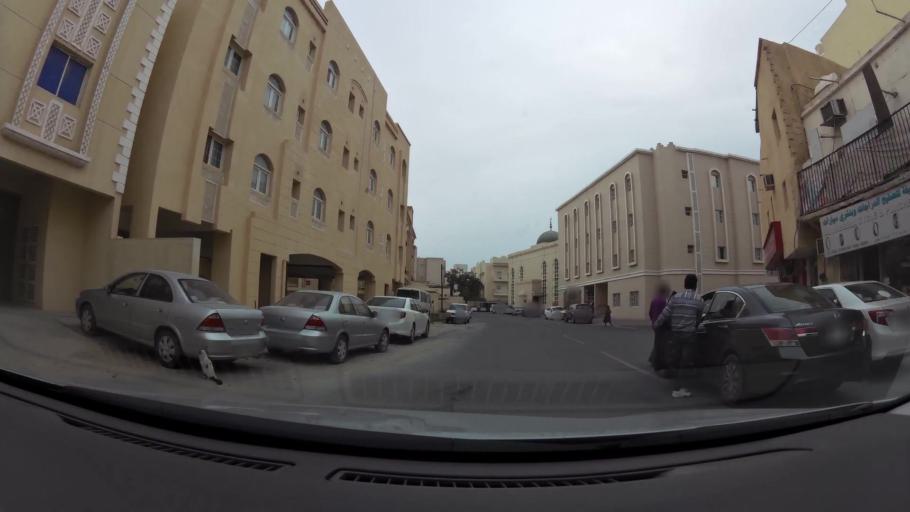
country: QA
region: Baladiyat ad Dawhah
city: Doha
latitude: 25.3035
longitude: 51.4945
